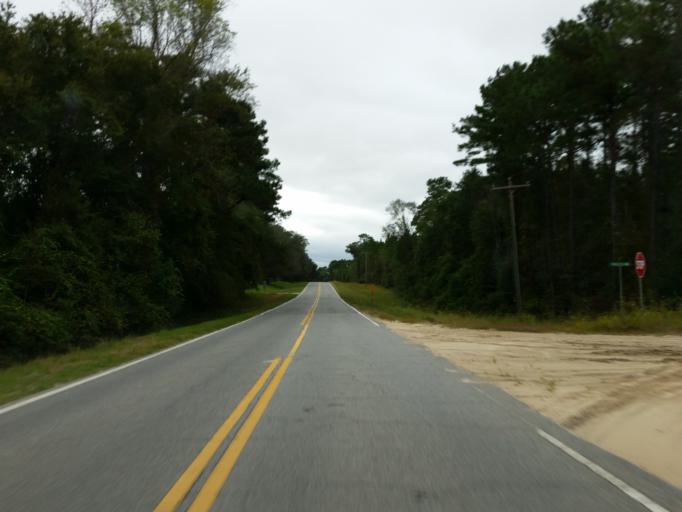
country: US
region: Georgia
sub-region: Echols County
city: Statenville
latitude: 30.8631
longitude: -83.0010
